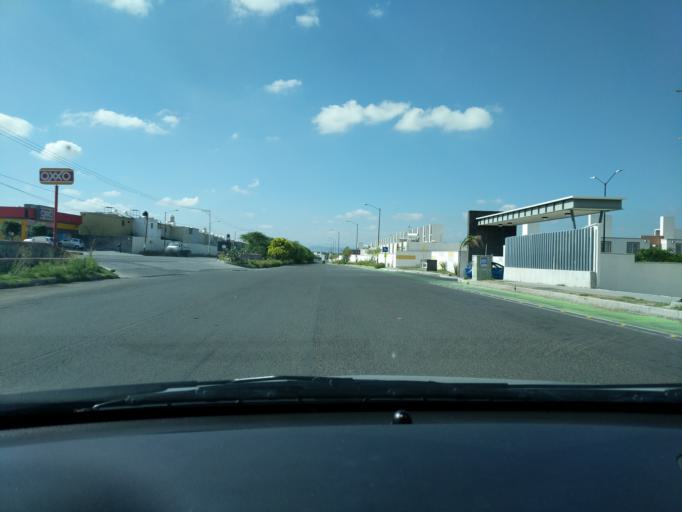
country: MX
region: Queretaro
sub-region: Queretaro
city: Patria Nueva
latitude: 20.6384
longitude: -100.4904
